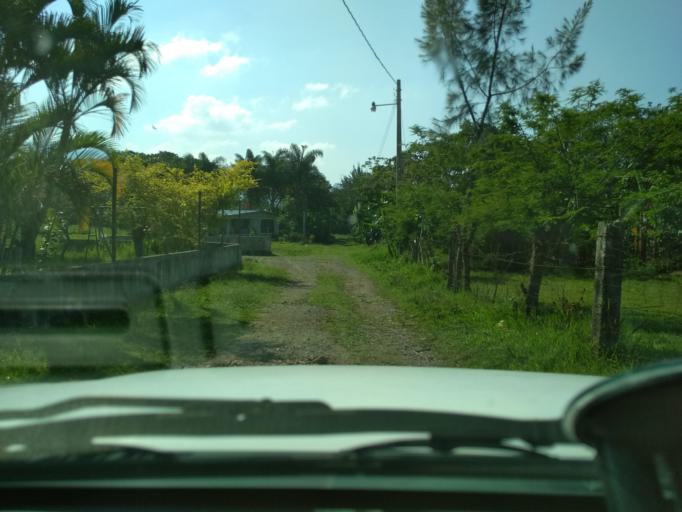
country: MX
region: Veracruz
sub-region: Chocaman
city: San Jose Neria
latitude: 18.9952
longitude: -96.9998
